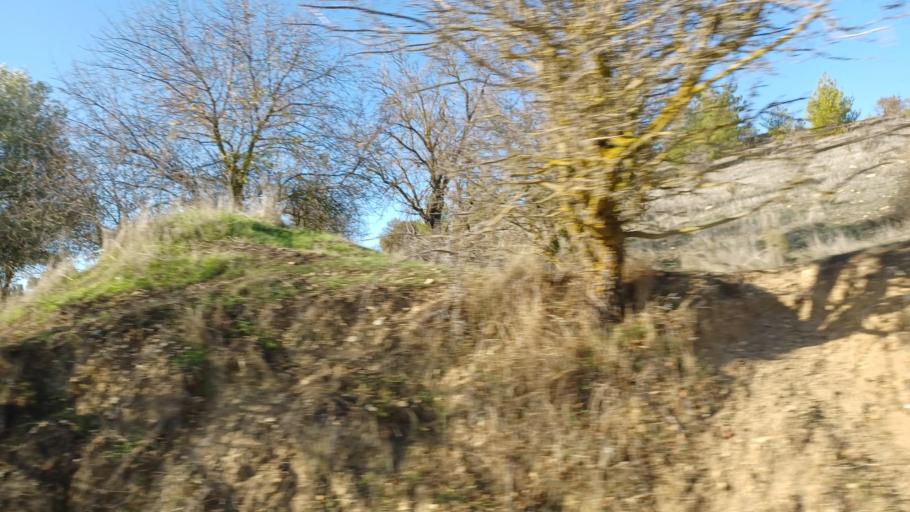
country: CY
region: Limassol
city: Pachna
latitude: 34.8424
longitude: 32.6817
